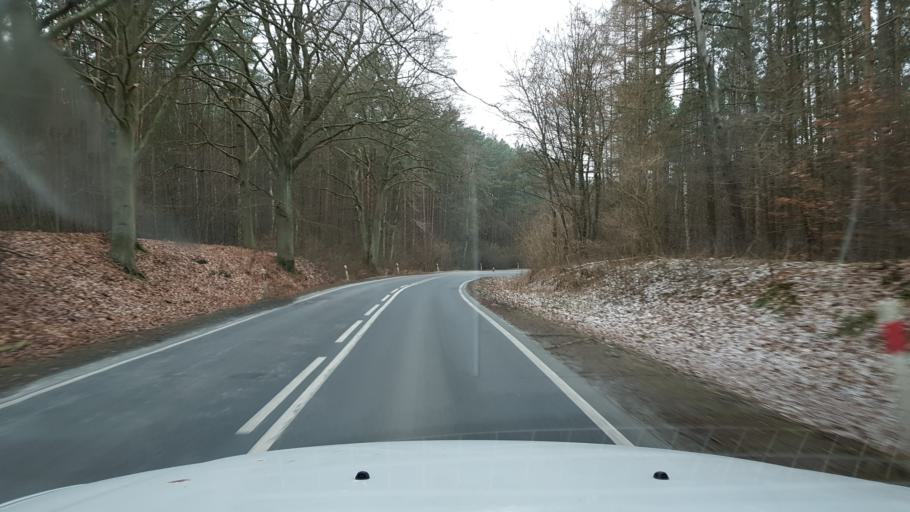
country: PL
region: West Pomeranian Voivodeship
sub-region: Powiat gryfinski
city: Gryfino
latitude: 53.1920
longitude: 14.5271
